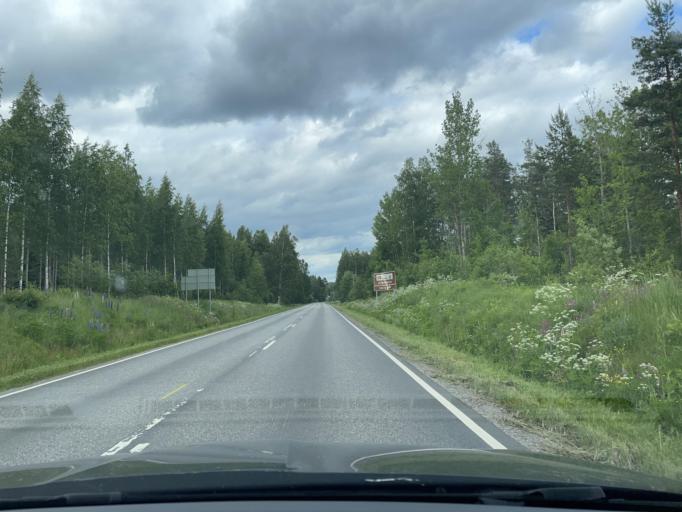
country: FI
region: Central Finland
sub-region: Jyvaeskylae
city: Petaejaevesi
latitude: 62.2435
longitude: 25.1663
